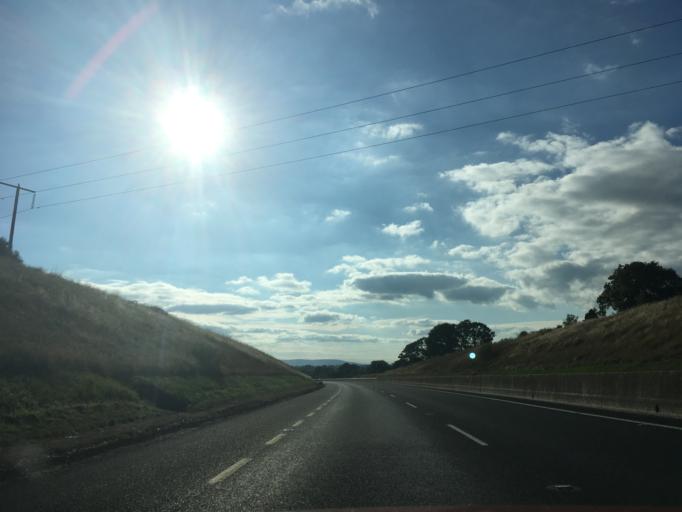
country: IE
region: Munster
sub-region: Waterford
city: Waterford
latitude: 52.2894
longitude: -7.1033
